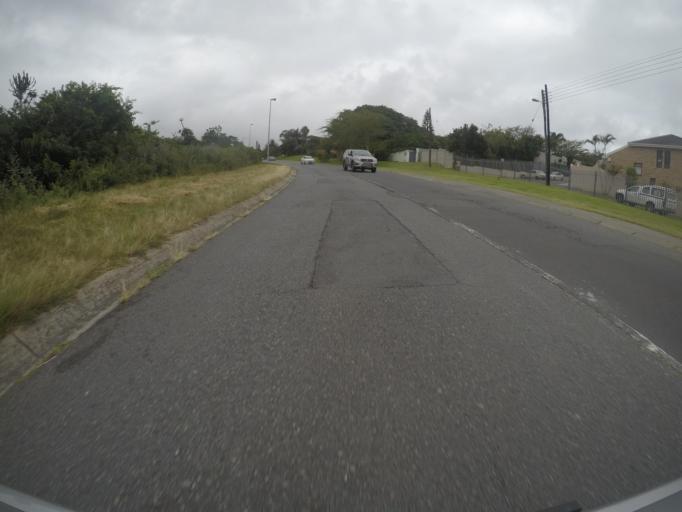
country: ZA
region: Eastern Cape
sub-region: Buffalo City Metropolitan Municipality
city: East London
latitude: -32.9800
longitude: 27.9387
